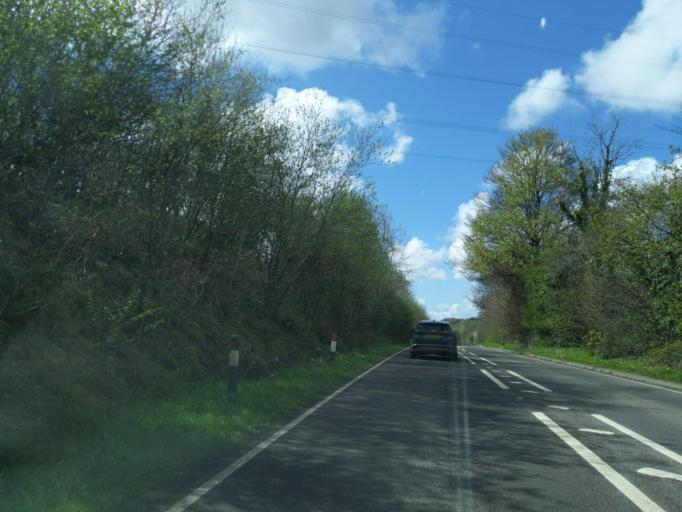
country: GB
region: England
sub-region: Cornwall
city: Wadebridge
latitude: 50.5072
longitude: -4.7912
